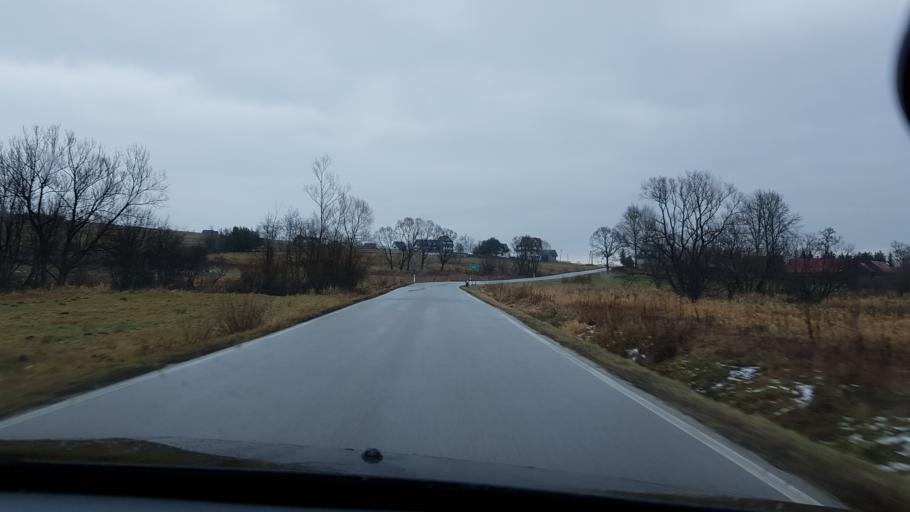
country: PL
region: Lesser Poland Voivodeship
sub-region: Powiat nowotarski
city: Czarny Dunajec
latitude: 49.4865
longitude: 19.8871
